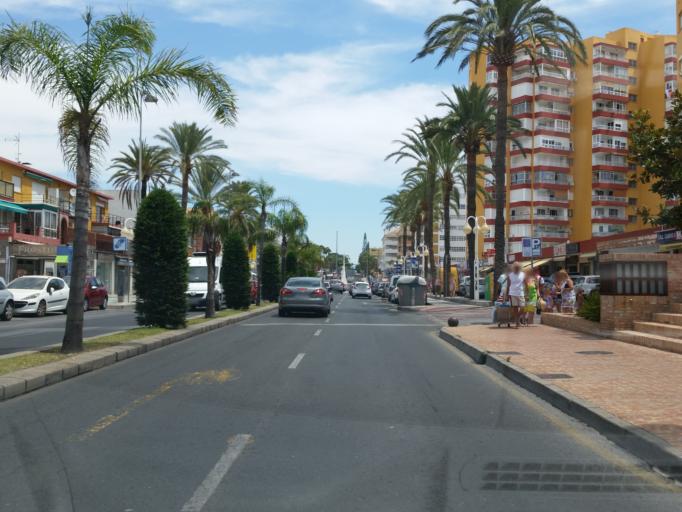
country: ES
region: Andalusia
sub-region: Provincia de Malaga
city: Torremolinos
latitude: 36.5976
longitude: -4.5186
